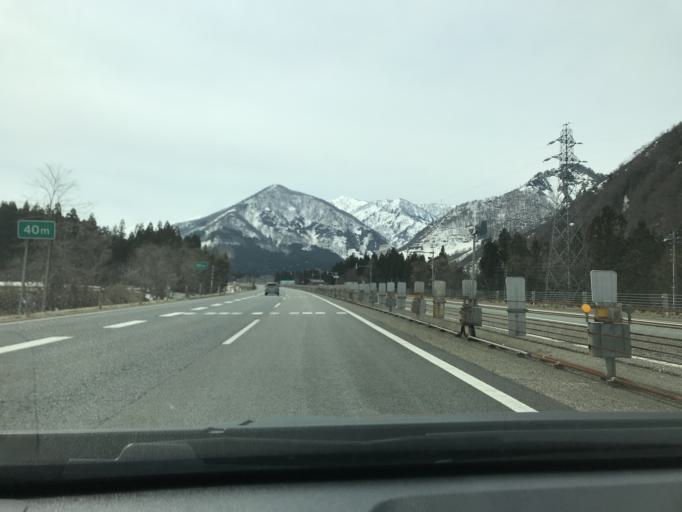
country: JP
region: Niigata
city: Shiozawa
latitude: 36.9210
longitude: 138.8437
